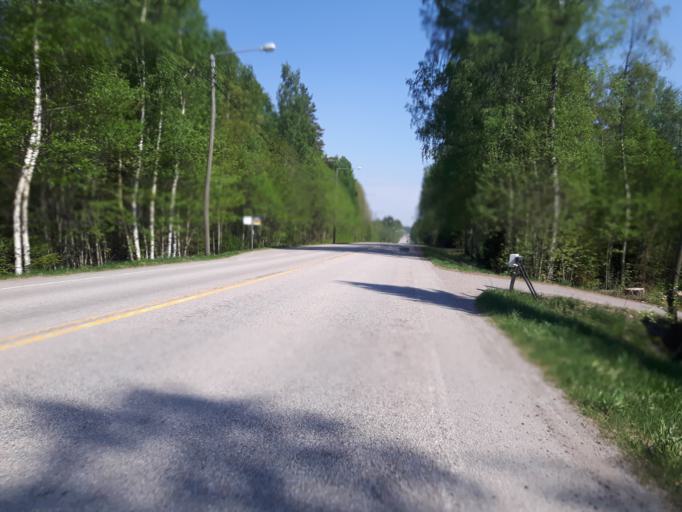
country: FI
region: Uusimaa
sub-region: Helsinki
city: Nickby
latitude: 60.3007
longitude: 25.3633
